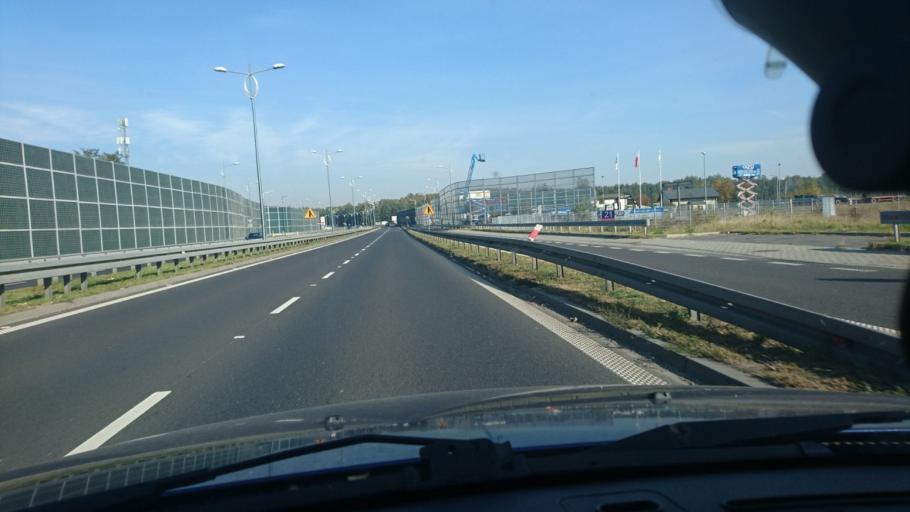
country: PL
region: Silesian Voivodeship
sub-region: Tychy
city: Cielmice
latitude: 50.1345
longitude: 19.0255
